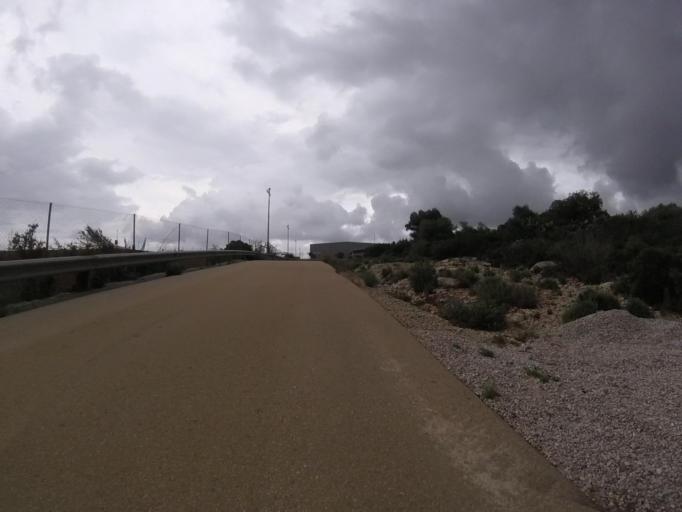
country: ES
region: Valencia
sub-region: Provincia de Castello
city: Benlloch
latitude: 40.2040
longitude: 0.0629
